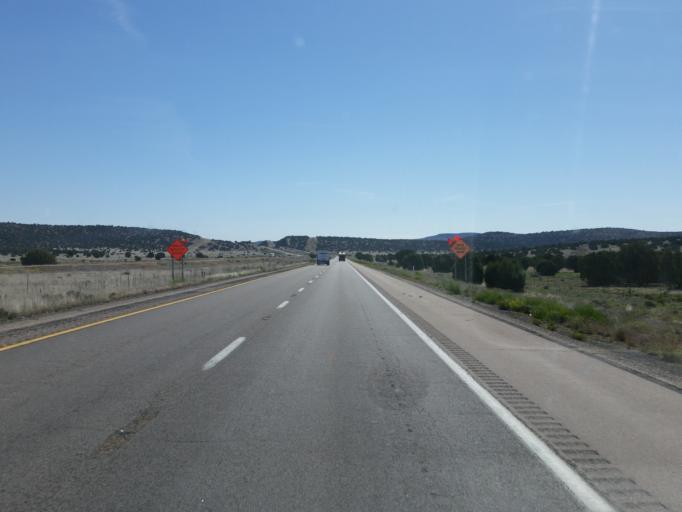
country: US
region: Arizona
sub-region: Mohave County
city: Peach Springs
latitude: 35.2291
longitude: -113.2259
